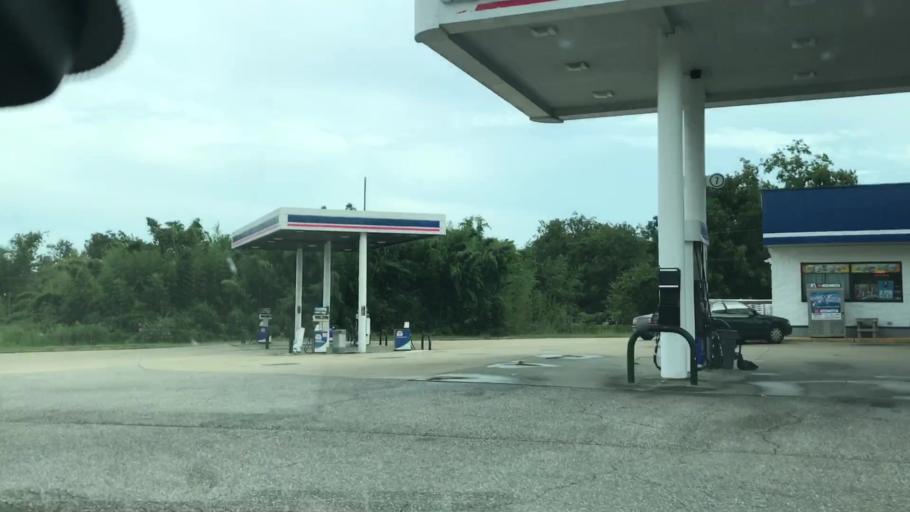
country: US
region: Georgia
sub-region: Quitman County
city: Georgetown
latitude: 31.8875
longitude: -85.1082
